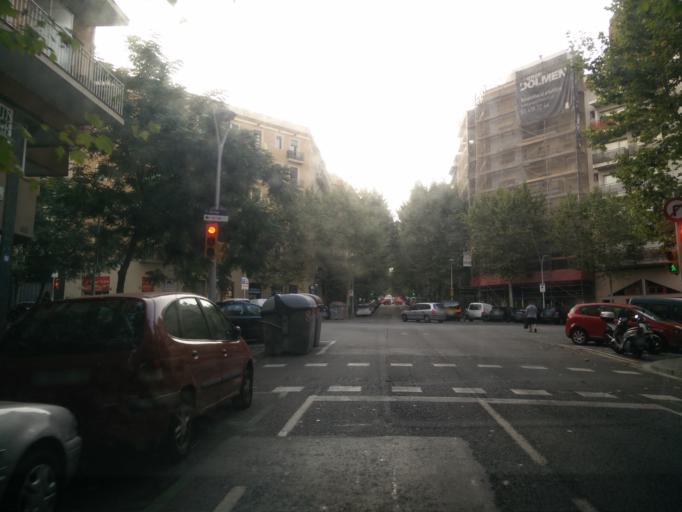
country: ES
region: Catalonia
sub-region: Provincia de Barcelona
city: Horta-Guinardo
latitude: 41.4092
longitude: 2.1768
